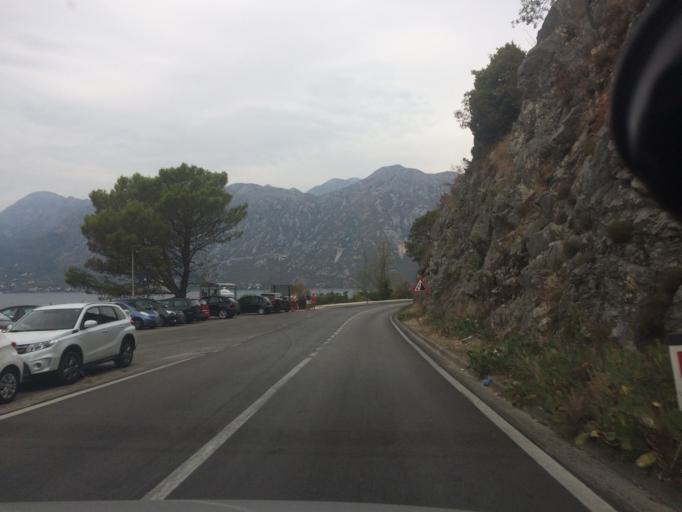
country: ME
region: Kotor
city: Risan
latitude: 42.4896
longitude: 18.6938
